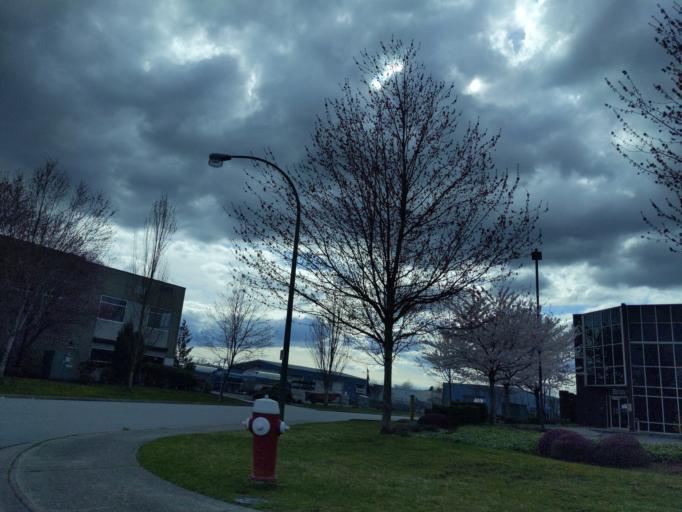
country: CA
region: British Columbia
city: Pitt Meadows
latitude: 49.2120
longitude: -122.6615
